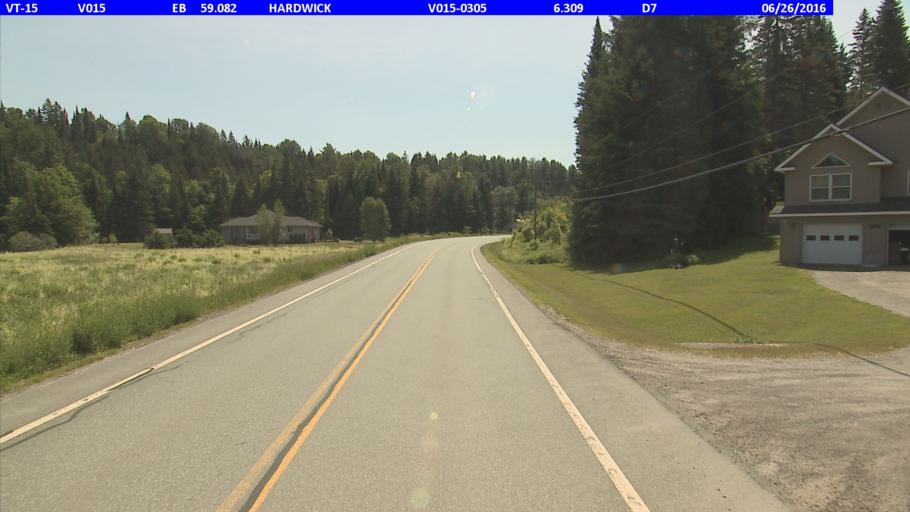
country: US
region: Vermont
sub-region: Caledonia County
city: Hardwick
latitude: 44.4942
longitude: -72.3160
